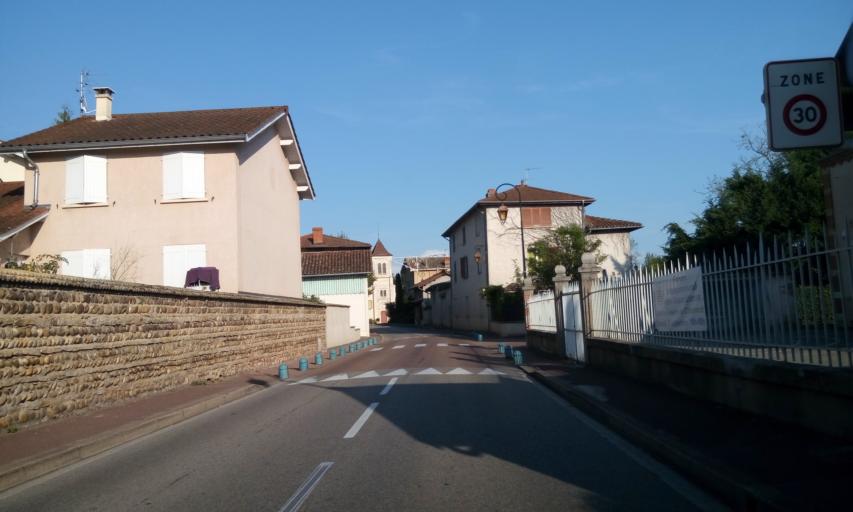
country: FR
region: Rhone-Alpes
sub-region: Departement de l'Ain
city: Chalamont
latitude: 45.9801
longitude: 5.1030
